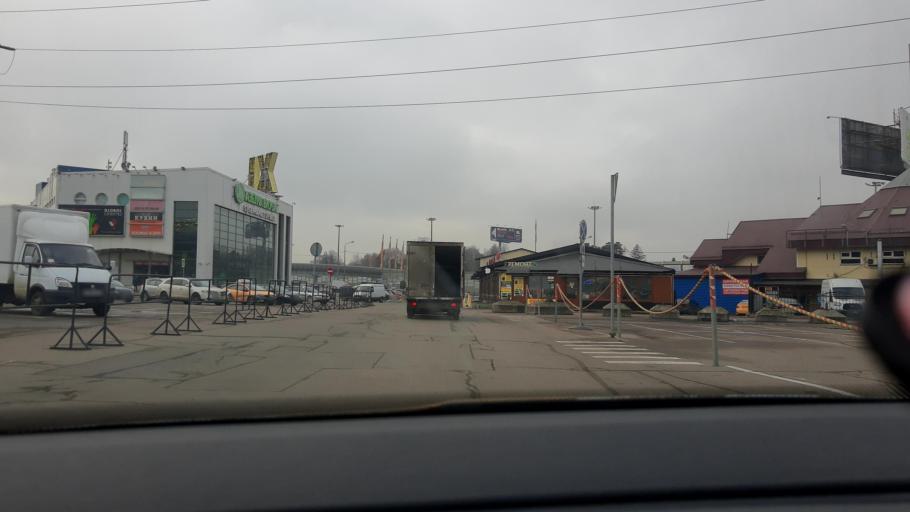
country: RU
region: Moskovskaya
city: Druzhba
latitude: 55.8927
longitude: 37.7476
